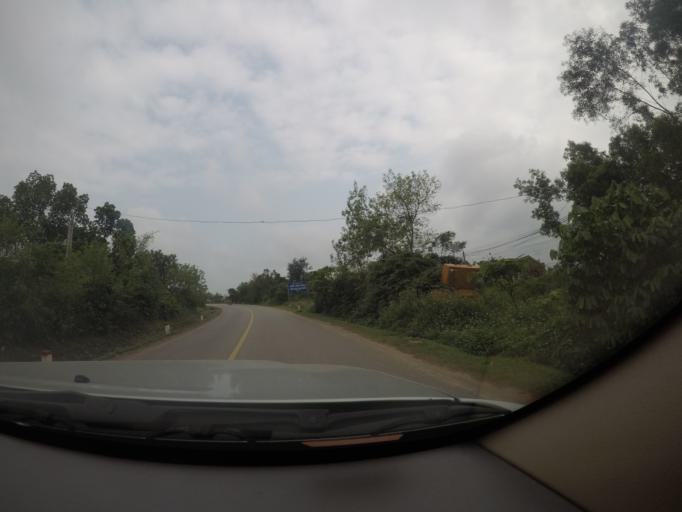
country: VN
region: Quang Binh
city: Kwang Binh
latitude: 17.4846
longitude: 106.5297
